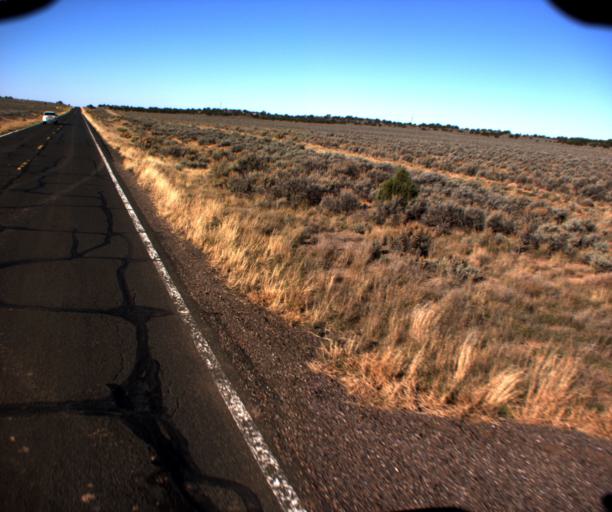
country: US
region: Arizona
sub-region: Navajo County
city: First Mesa
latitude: 35.7444
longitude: -110.0619
